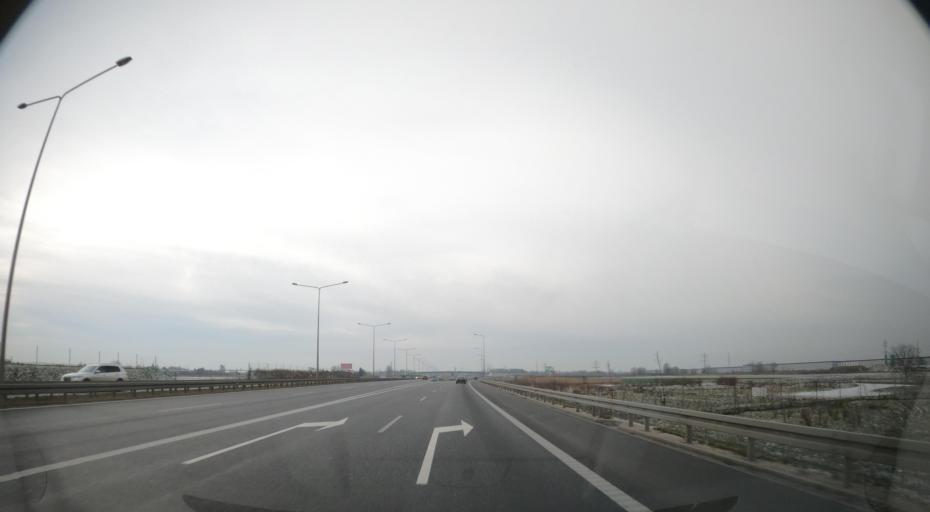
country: PL
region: Masovian Voivodeship
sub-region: Powiat pruszkowski
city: Michalowice
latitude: 52.1361
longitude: 20.8804
